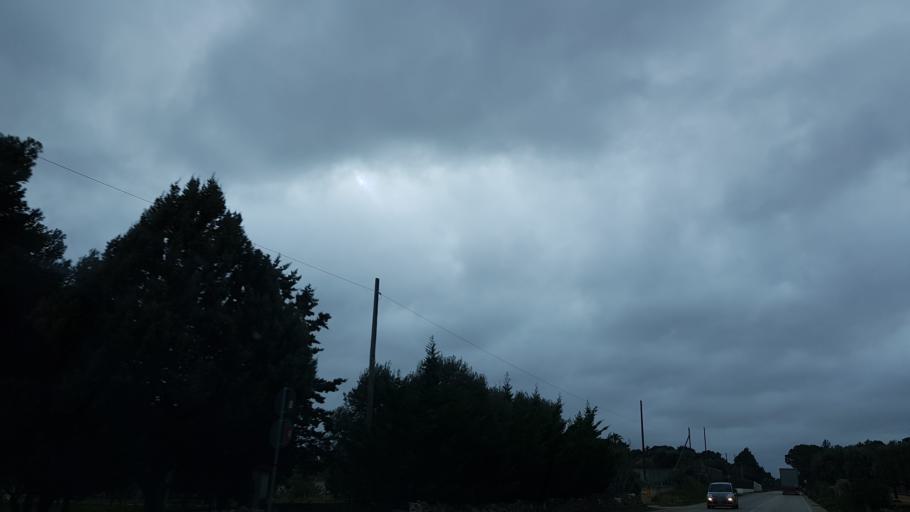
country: IT
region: Apulia
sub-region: Provincia di Brindisi
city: San Vito dei Normanni
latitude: 40.6544
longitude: 17.7708
